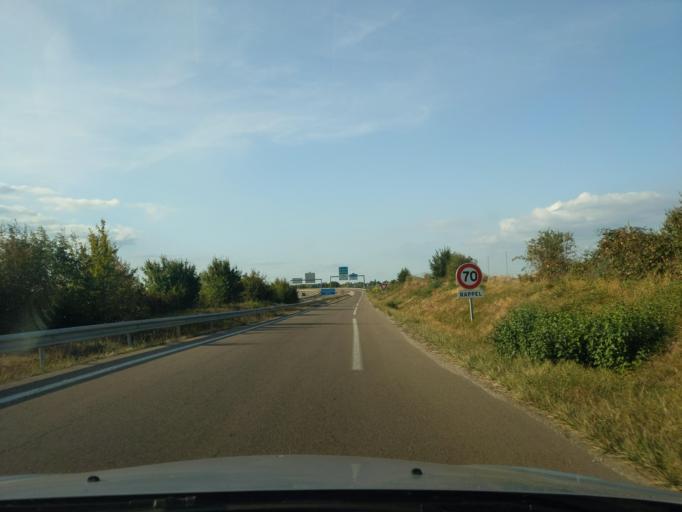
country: FR
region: Bourgogne
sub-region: Departement de la Cote-d'Or
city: Longvic
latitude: 47.2969
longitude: 5.0832
